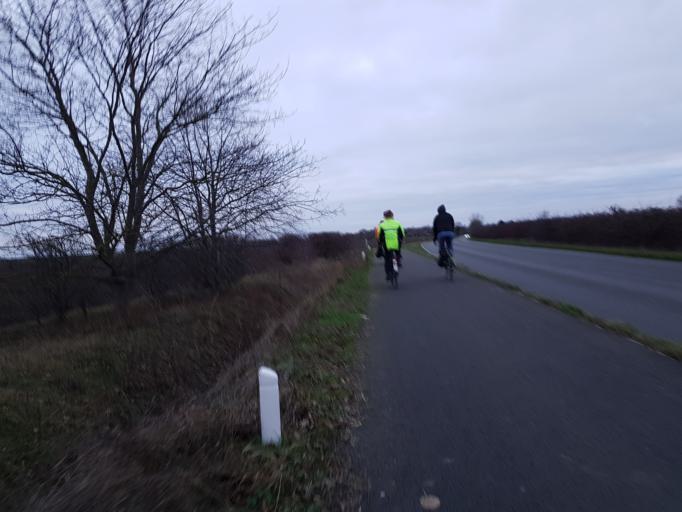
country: GB
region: England
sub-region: Cambridgeshire
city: Bottisham
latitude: 52.2290
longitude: 0.2336
